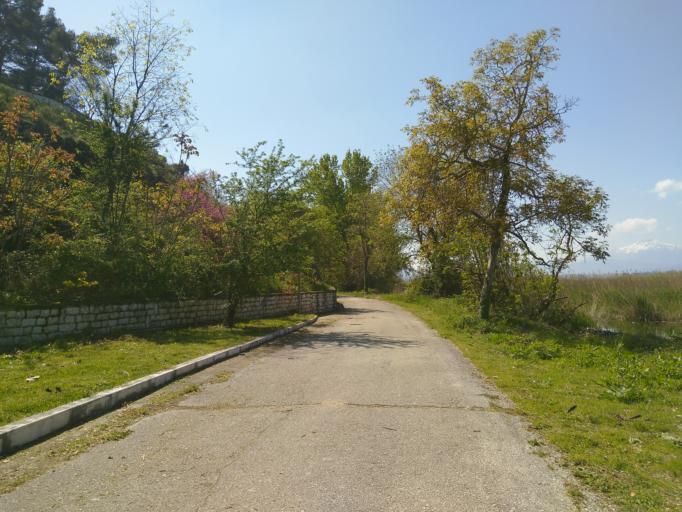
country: GR
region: Epirus
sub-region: Nomos Ioanninon
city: Ioannina
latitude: 39.6788
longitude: 20.8724
